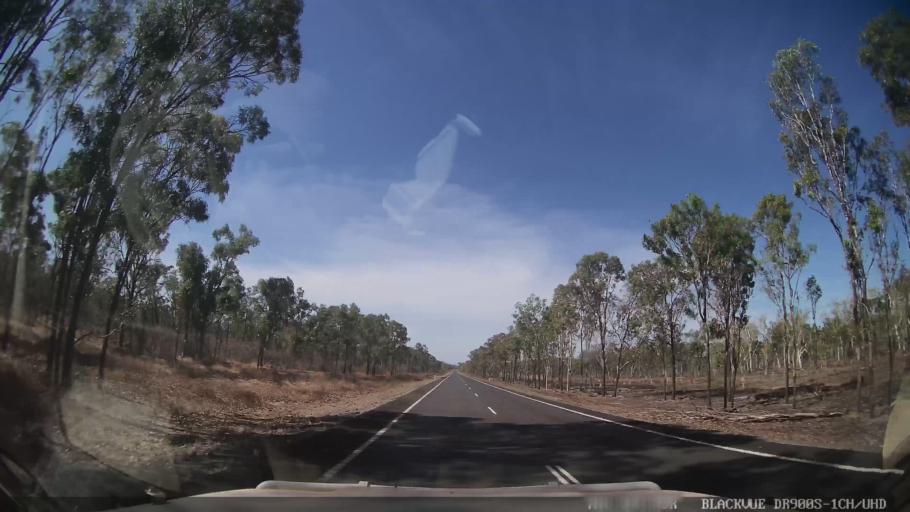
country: AU
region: Queensland
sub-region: Cook
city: Cooktown
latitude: -15.7864
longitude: 144.9532
